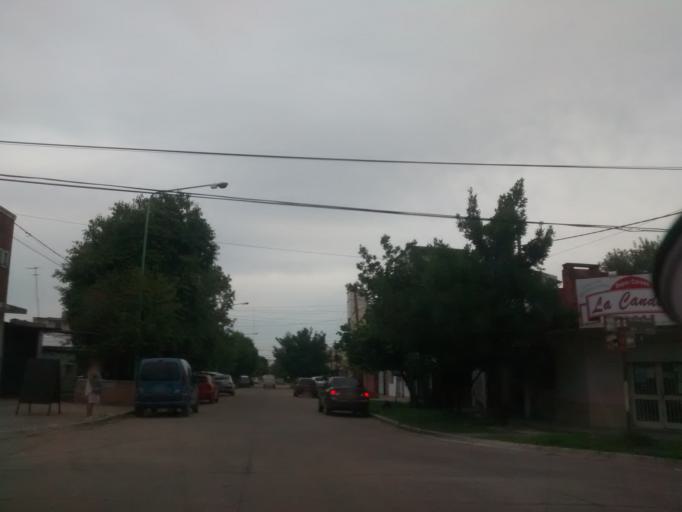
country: AR
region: Chaco
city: Resistencia
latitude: -27.4622
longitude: -58.9901
